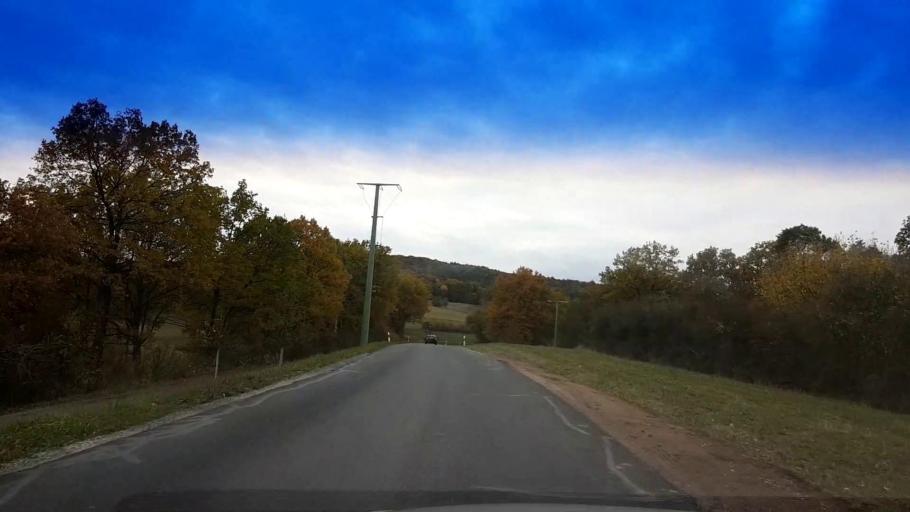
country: DE
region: Bavaria
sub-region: Upper Franconia
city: Viereth-Trunstadt
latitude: 49.9171
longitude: 10.7663
